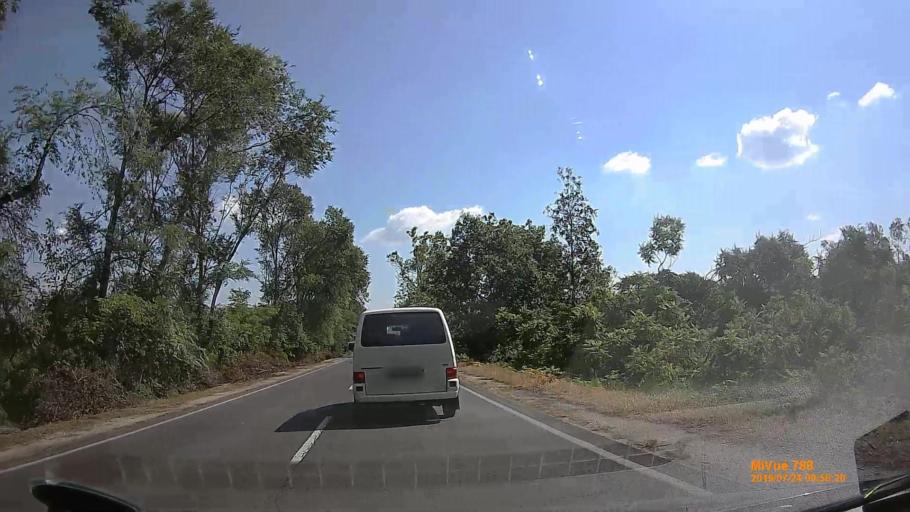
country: HU
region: Szabolcs-Szatmar-Bereg
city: Nyirmada
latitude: 48.0643
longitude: 22.2225
